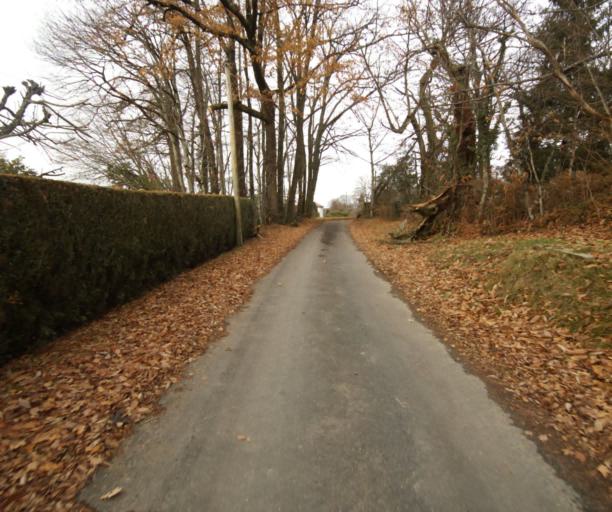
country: FR
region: Limousin
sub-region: Departement de la Correze
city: Chameyrat
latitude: 45.2650
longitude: 1.7150
